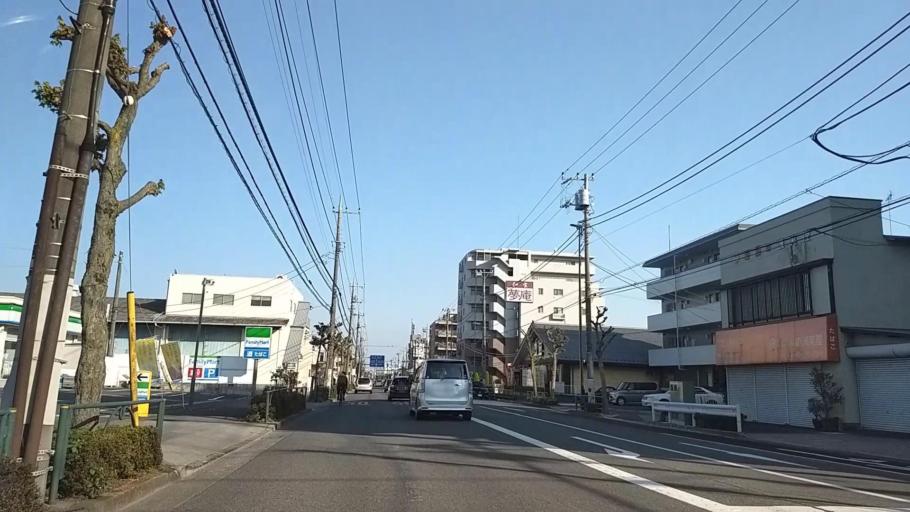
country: JP
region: Tokyo
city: Ome
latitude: 35.7884
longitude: 139.2900
